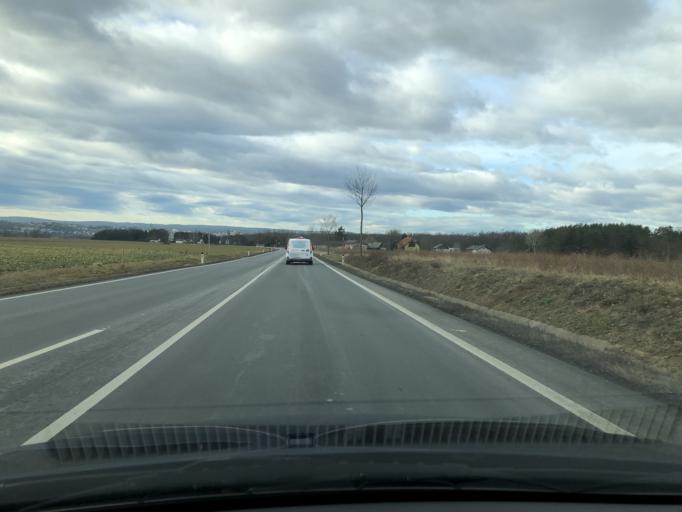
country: AT
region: Burgenland
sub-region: Politischer Bezirk Oberwart
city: Grosspetersdorf
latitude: 47.2583
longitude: 16.3538
